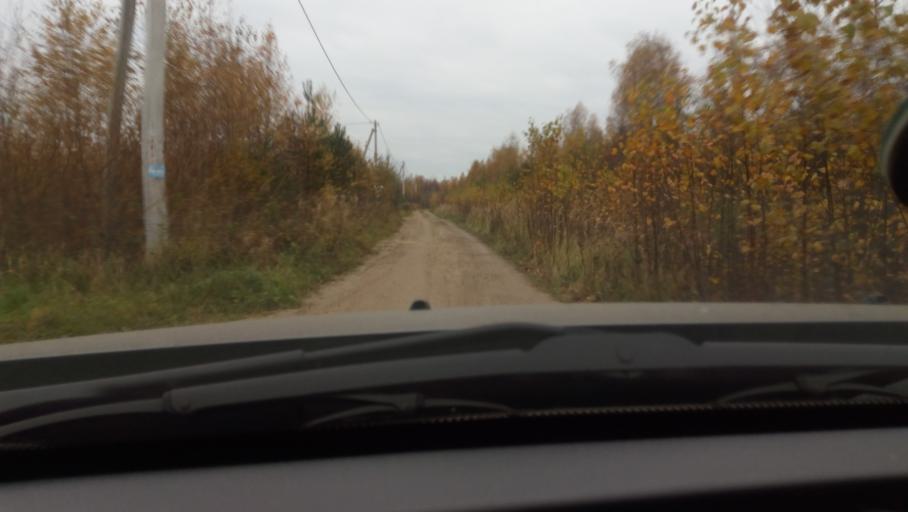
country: RU
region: Moskovskaya
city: Avsyunino
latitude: 55.5804
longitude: 39.2483
